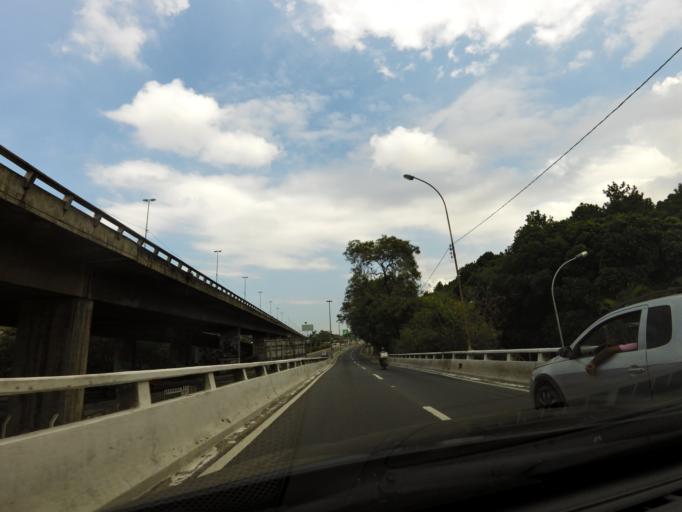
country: BR
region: Espirito Santo
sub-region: Vitoria
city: Vitoria
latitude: -20.3301
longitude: -40.3549
